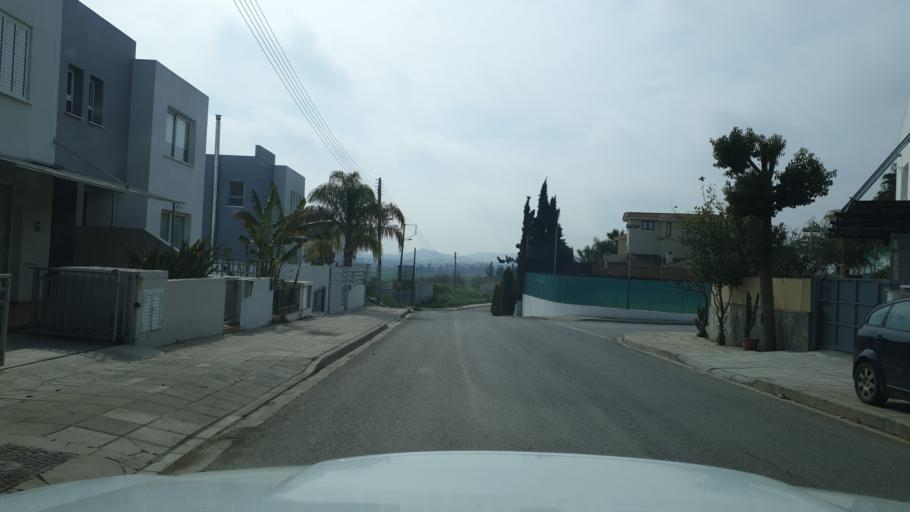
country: CY
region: Lefkosia
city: Tseri
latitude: 35.1204
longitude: 33.3503
